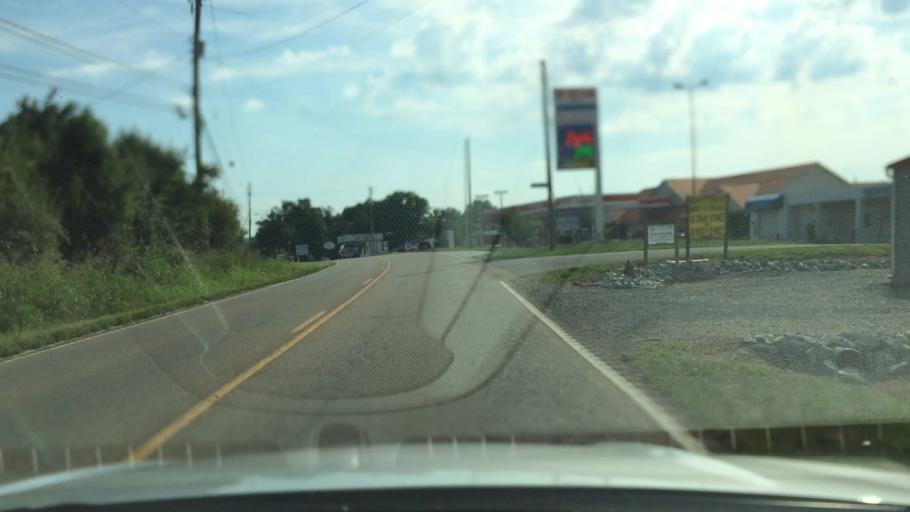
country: US
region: Tennessee
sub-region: Sevier County
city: Seymour
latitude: 35.9171
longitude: -83.6705
